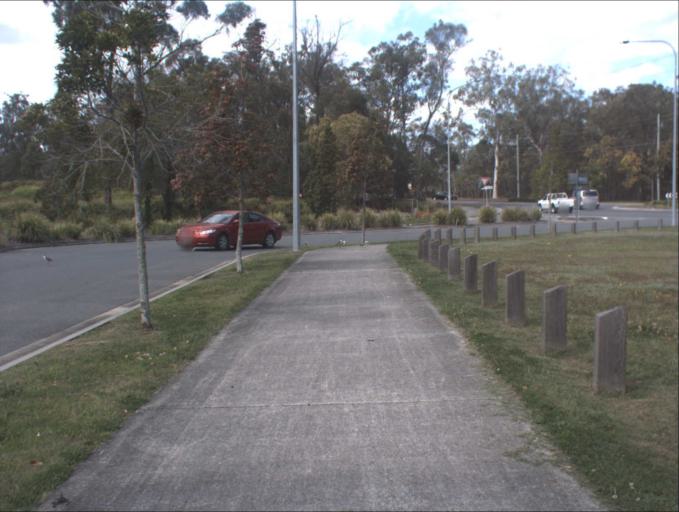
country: AU
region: Queensland
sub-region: Logan
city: Woodridge
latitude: -27.6715
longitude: 153.0751
